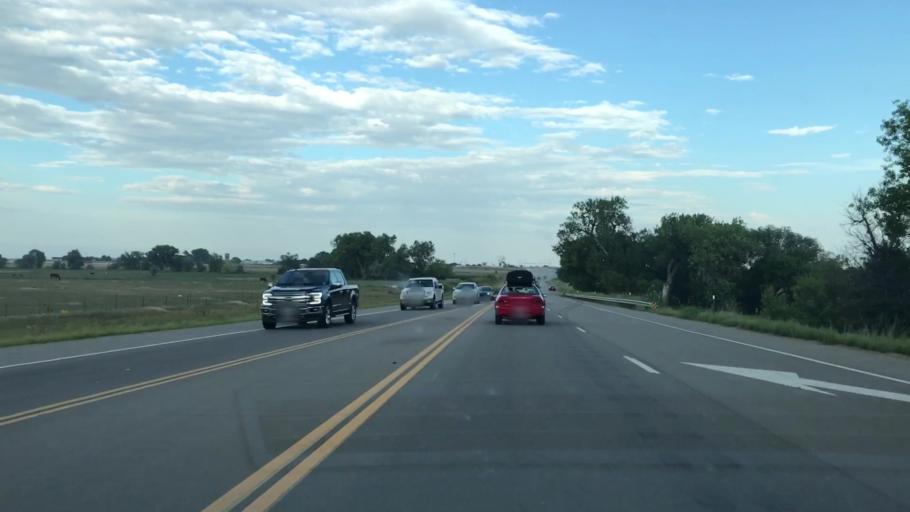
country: US
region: Colorado
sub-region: Weld County
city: Mead
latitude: 40.2045
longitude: -104.9959
